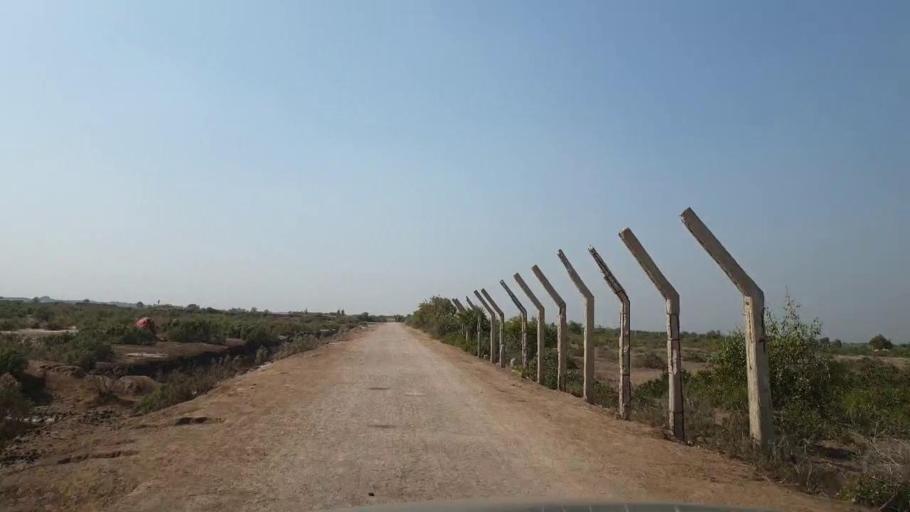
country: PK
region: Sindh
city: Tando Allahyar
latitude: 25.5529
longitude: 68.7024
